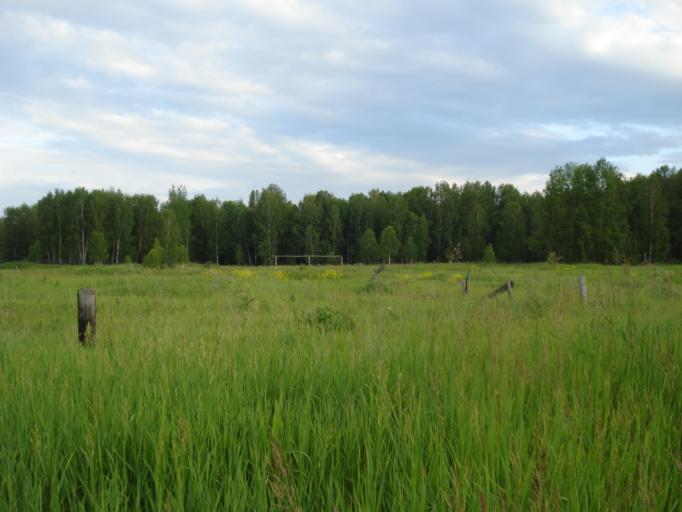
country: RU
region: Krasnoyarskiy
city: Predivinsk
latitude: 56.9731
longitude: 92.8731
